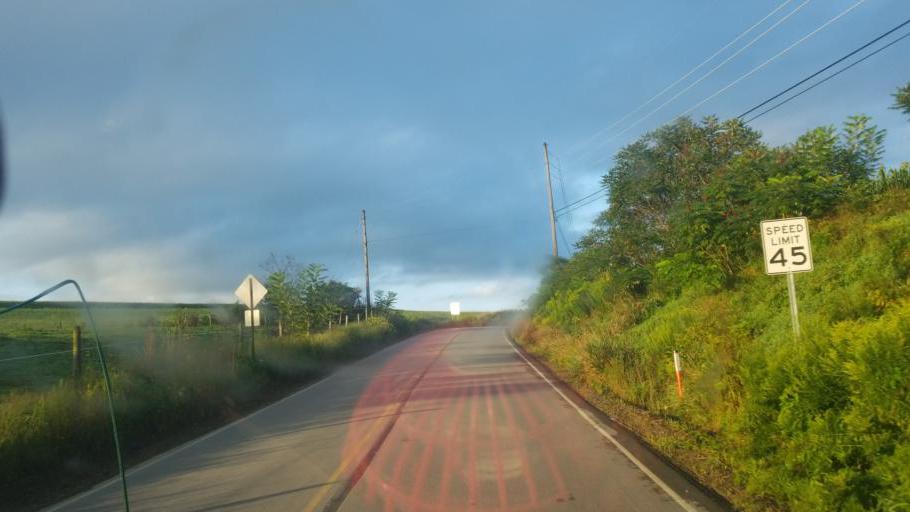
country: US
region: Pennsylvania
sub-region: Potter County
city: Galeton
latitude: 41.8925
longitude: -77.7600
